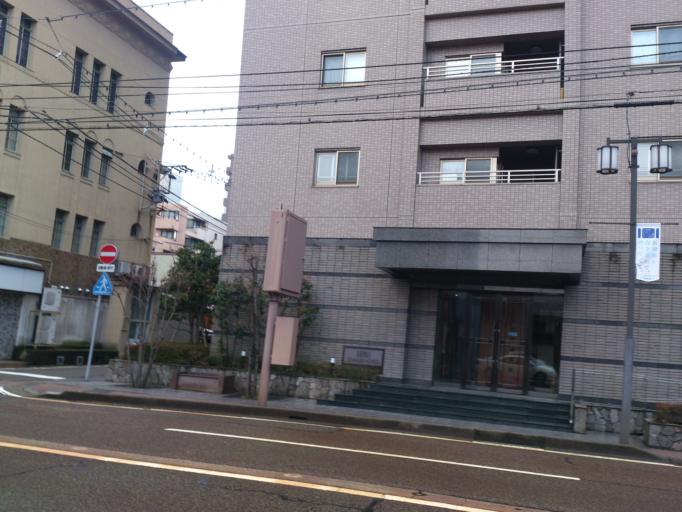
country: JP
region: Ishikawa
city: Kanazawa-shi
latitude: 36.5715
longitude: 136.6597
